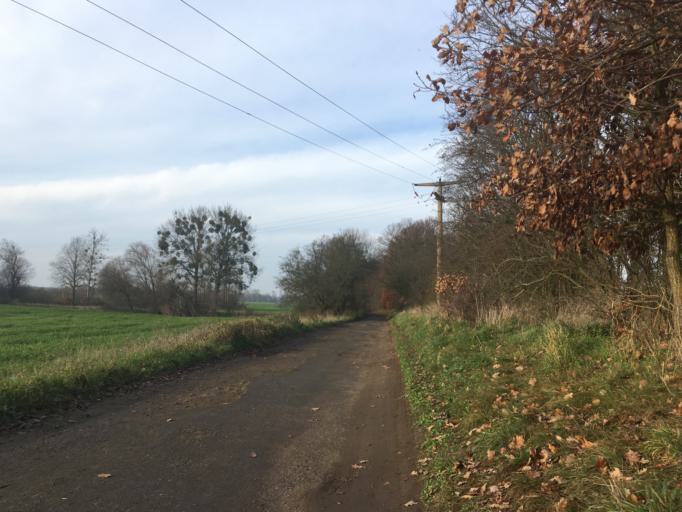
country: DE
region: Brandenburg
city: Bad Freienwalde
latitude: 52.8198
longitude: 14.0006
